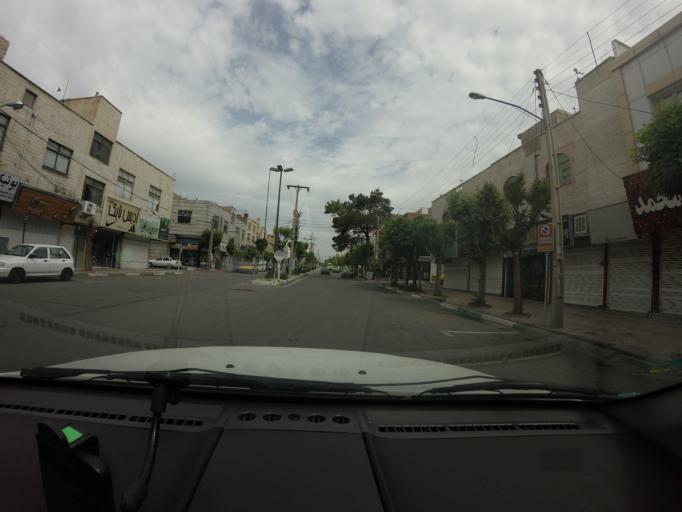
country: IR
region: Tehran
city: Eslamshahr
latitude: 35.5506
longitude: 51.2510
